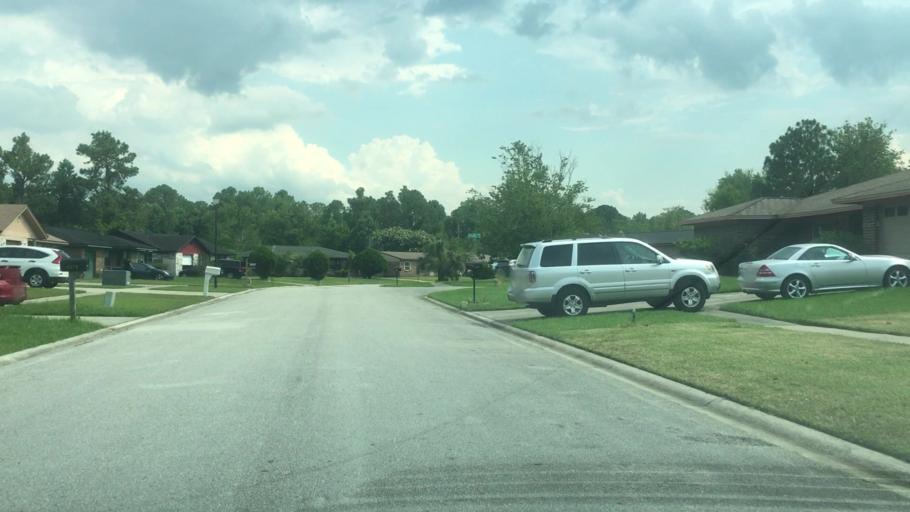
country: US
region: Florida
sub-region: Duval County
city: Neptune Beach
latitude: 30.3041
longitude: -81.5091
